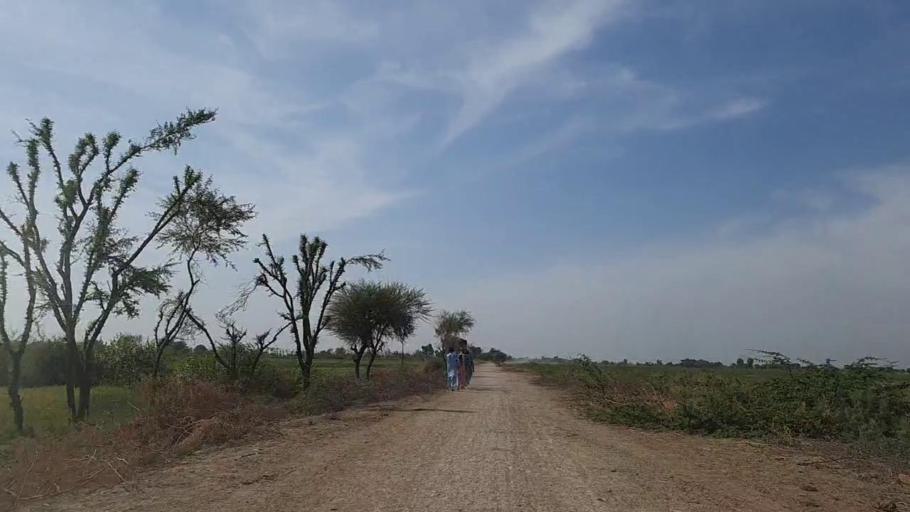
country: PK
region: Sindh
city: Samaro
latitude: 25.2090
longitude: 69.4396
